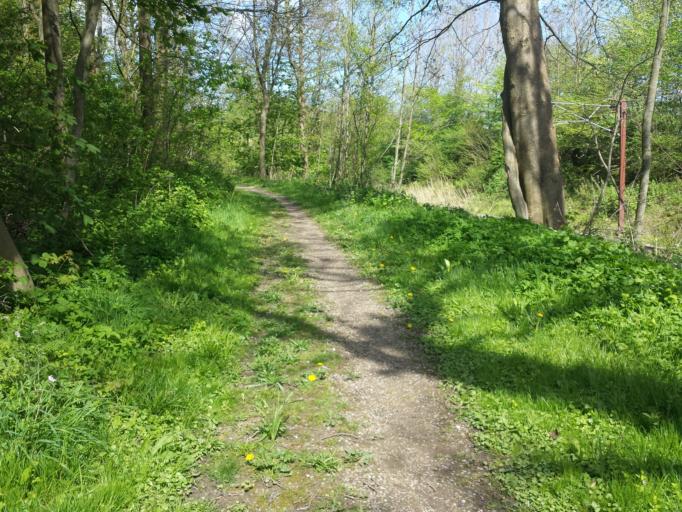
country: DK
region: South Denmark
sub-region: Sonderborg Kommune
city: Grasten
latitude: 54.9258
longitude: 9.6072
